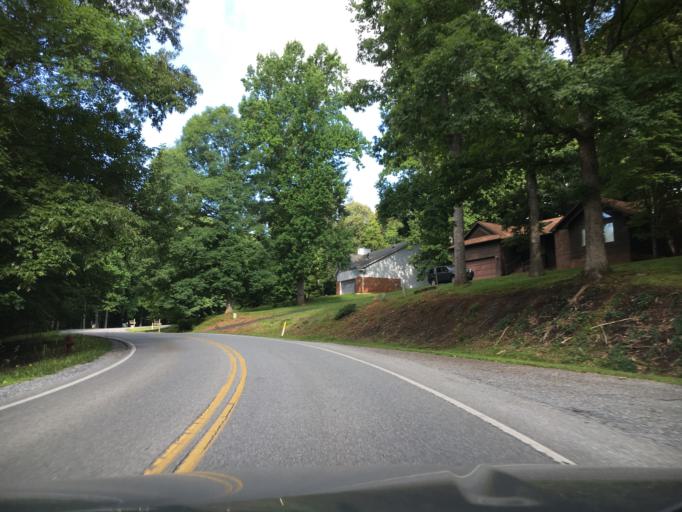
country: US
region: Virginia
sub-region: Bedford County
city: Forest
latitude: 37.3889
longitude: -79.2537
